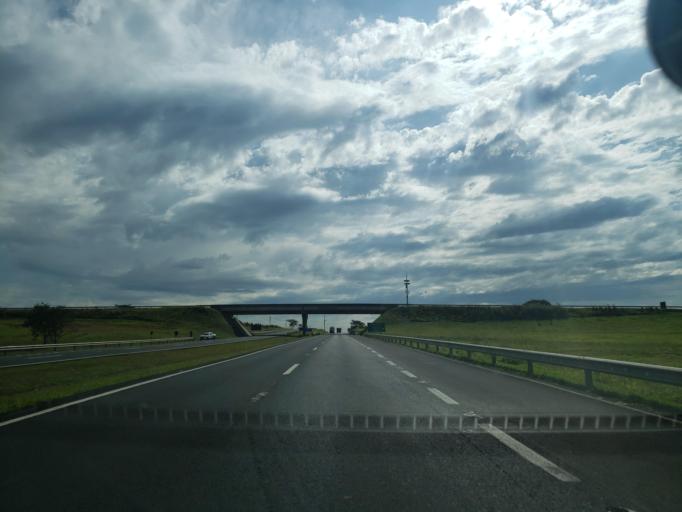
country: BR
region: Sao Paulo
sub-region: Cafelandia
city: Cafelandia
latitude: -21.8758
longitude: -49.5599
